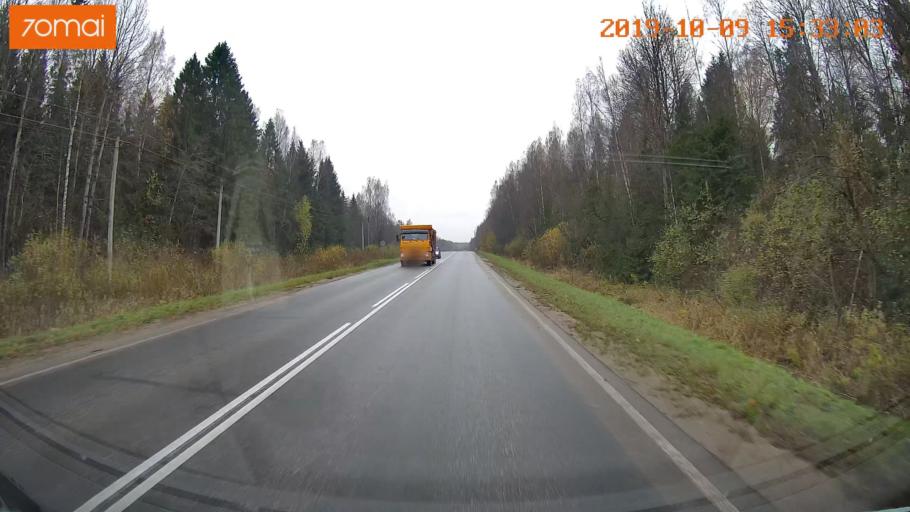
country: RU
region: Kostroma
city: Oktyabr'skiy
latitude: 57.9570
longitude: 41.2676
